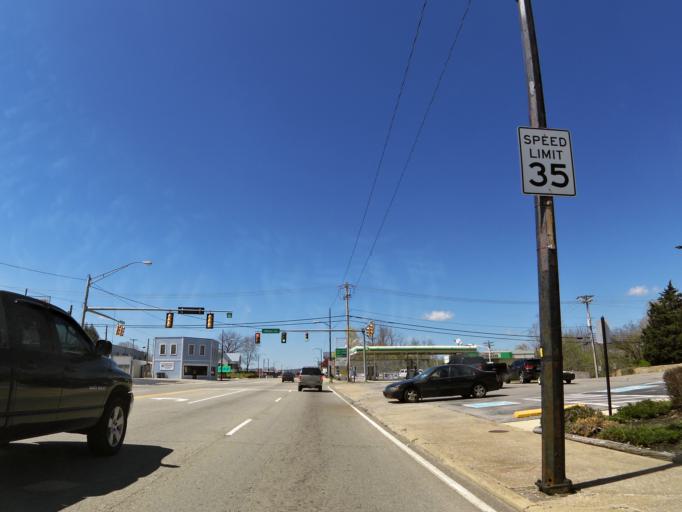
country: US
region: Tennessee
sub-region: White County
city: Sparta
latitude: 35.9285
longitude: -85.4700
